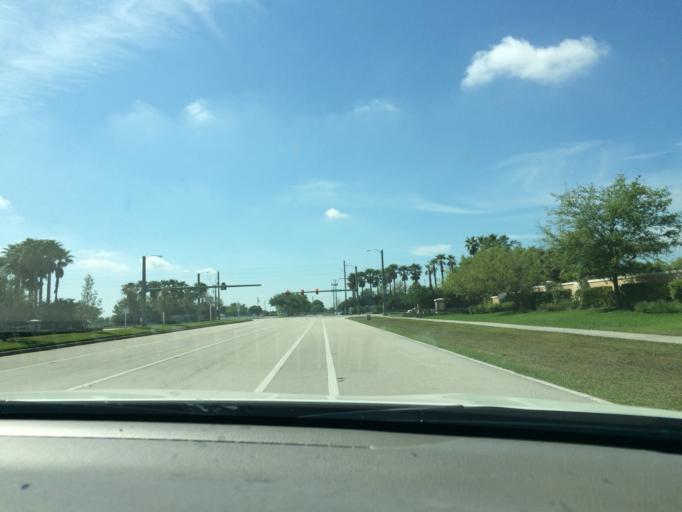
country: US
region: Florida
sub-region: Sarasota County
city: The Meadows
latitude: 27.3878
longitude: -82.3983
